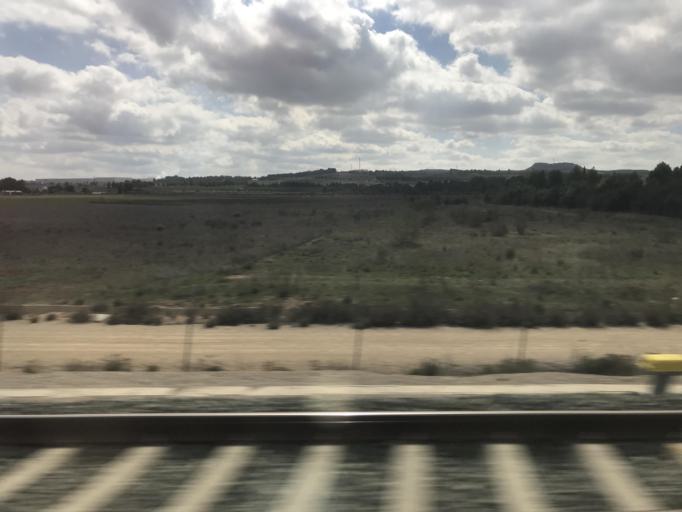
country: ES
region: Castille-La Mancha
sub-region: Provincia de Albacete
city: Almansa
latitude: 38.8871
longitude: -1.1336
